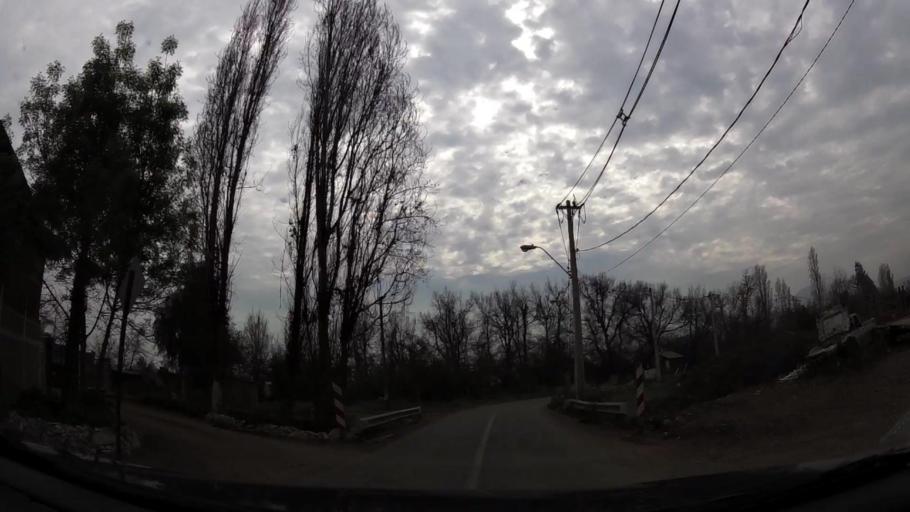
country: CL
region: Santiago Metropolitan
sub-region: Provincia de Chacabuco
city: Lampa
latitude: -33.2237
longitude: -70.7717
